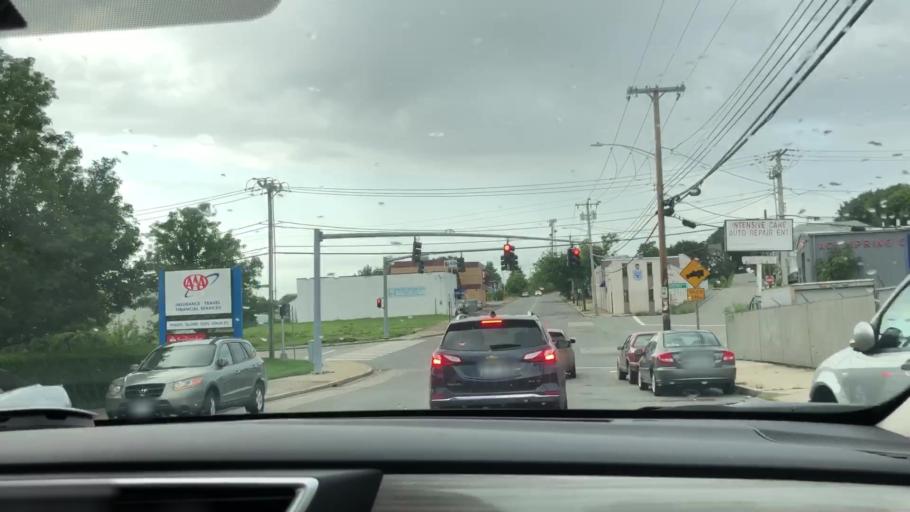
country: US
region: Rhode Island
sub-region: Providence County
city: Providence
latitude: 41.8521
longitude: -71.4130
